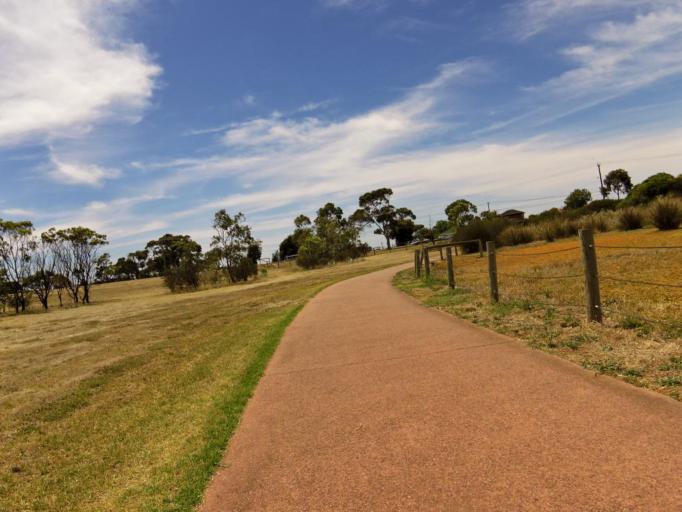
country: AU
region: Victoria
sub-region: Hobsons Bay
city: Seaholme
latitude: -37.8574
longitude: 144.8419
